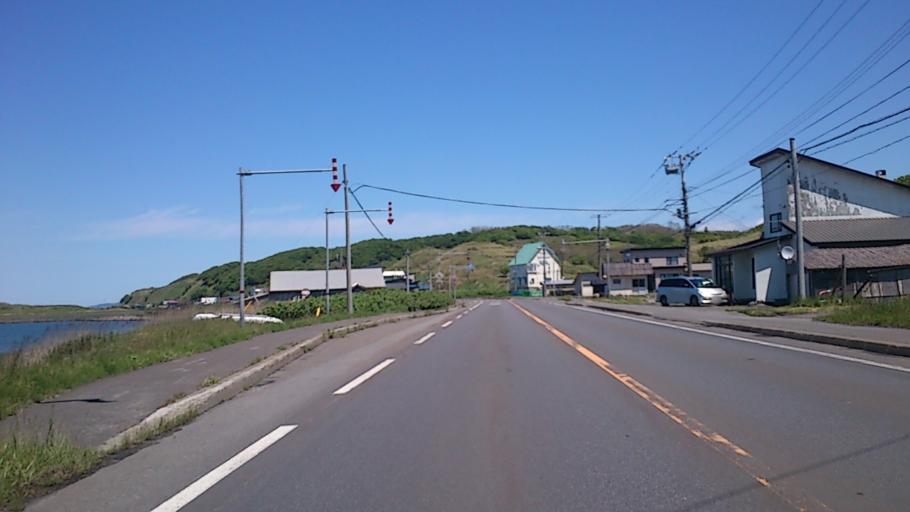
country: JP
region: Hokkaido
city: Rumoi
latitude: 43.9643
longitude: 141.6442
